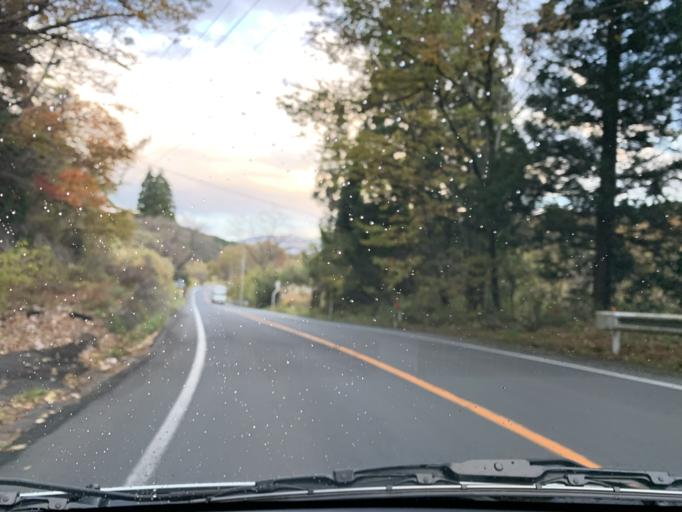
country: JP
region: Iwate
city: Mizusawa
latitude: 39.0645
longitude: 141.0668
